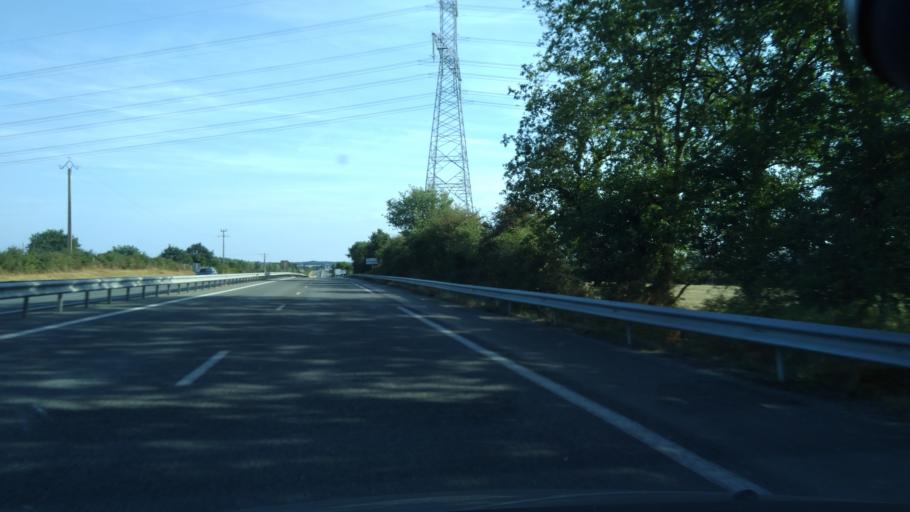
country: FR
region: Pays de la Loire
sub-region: Departement de la Mayenne
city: Entrammes
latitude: 47.9341
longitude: -0.6948
